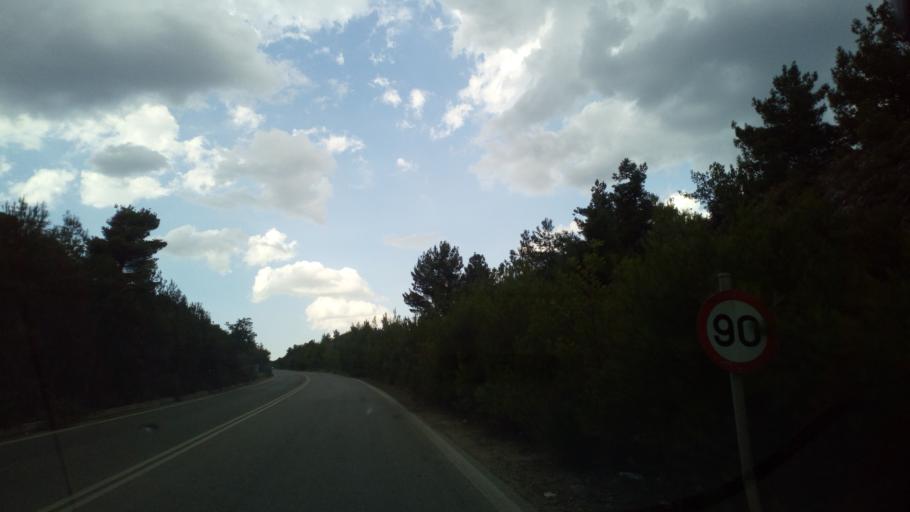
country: GR
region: Central Macedonia
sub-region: Nomos Chalkidikis
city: Polygyros
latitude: 40.3512
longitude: 23.4467
